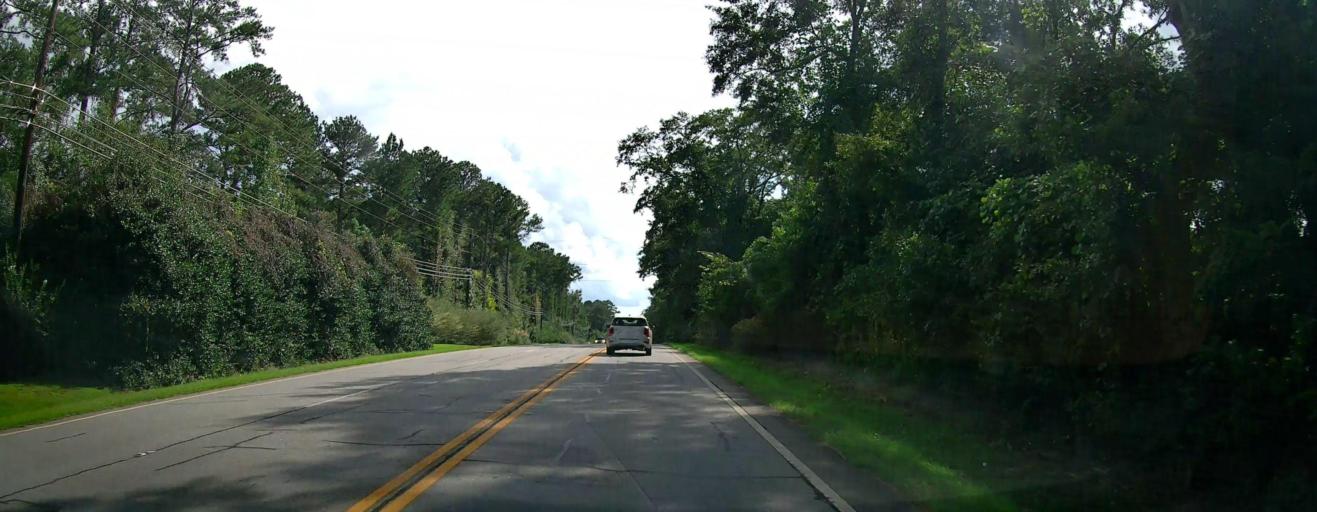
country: US
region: Georgia
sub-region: Harris County
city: Hamilton
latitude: 32.6167
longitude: -84.9069
